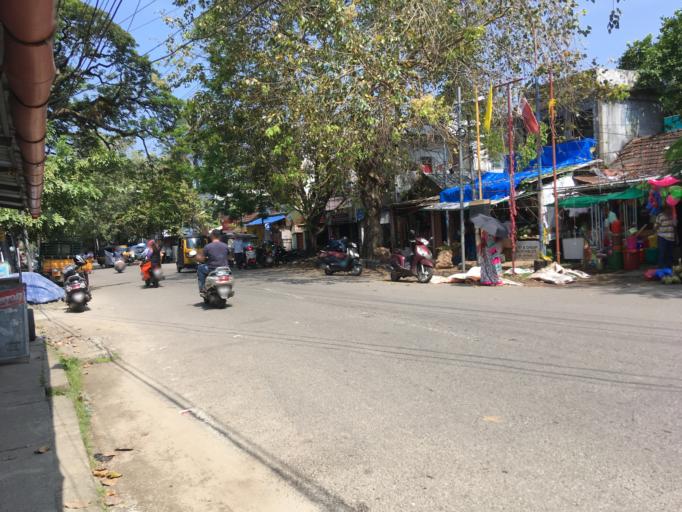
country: IN
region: Kerala
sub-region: Ernakulam
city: Cochin
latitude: 9.9580
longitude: 76.2450
